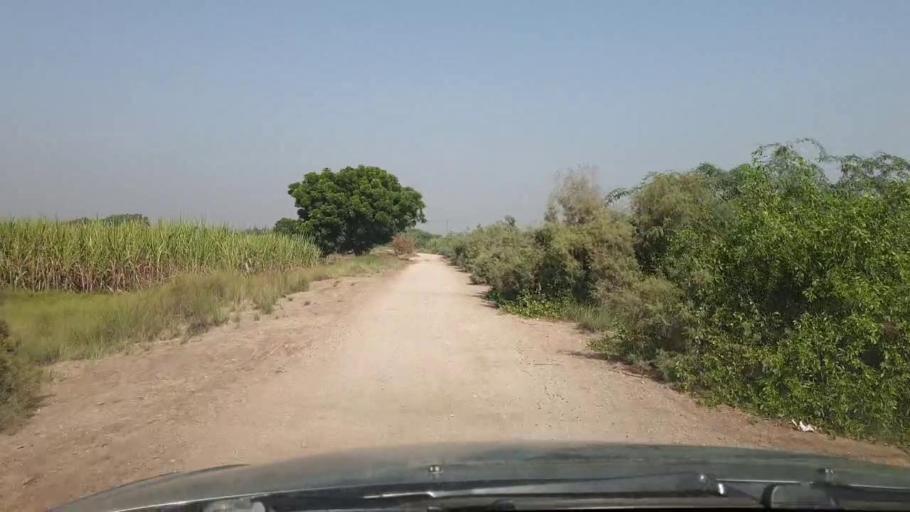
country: PK
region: Sindh
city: Tando Jam
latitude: 25.2819
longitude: 68.5345
